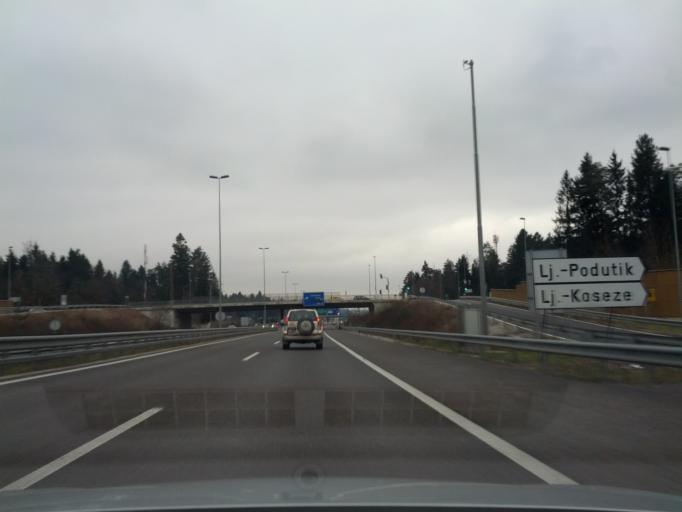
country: SI
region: Ljubljana
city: Ljubljana
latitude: 46.0755
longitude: 14.4597
